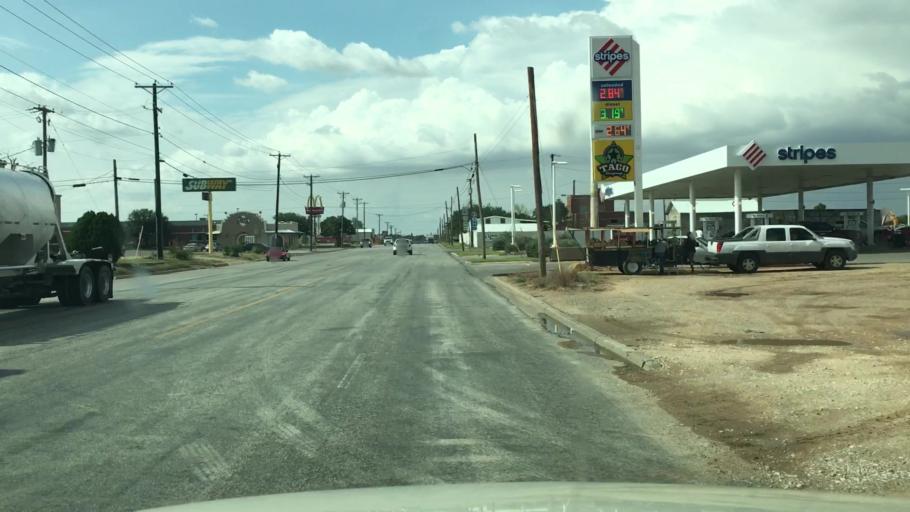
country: US
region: Texas
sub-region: Dawson County
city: Lamesa
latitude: 32.7359
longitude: -101.9499
